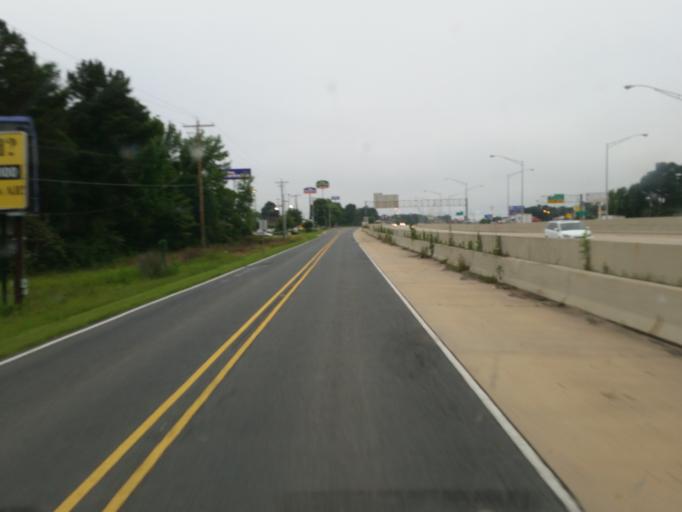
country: US
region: Louisiana
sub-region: Caddo Parish
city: Greenwood
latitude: 32.4525
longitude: -93.8551
